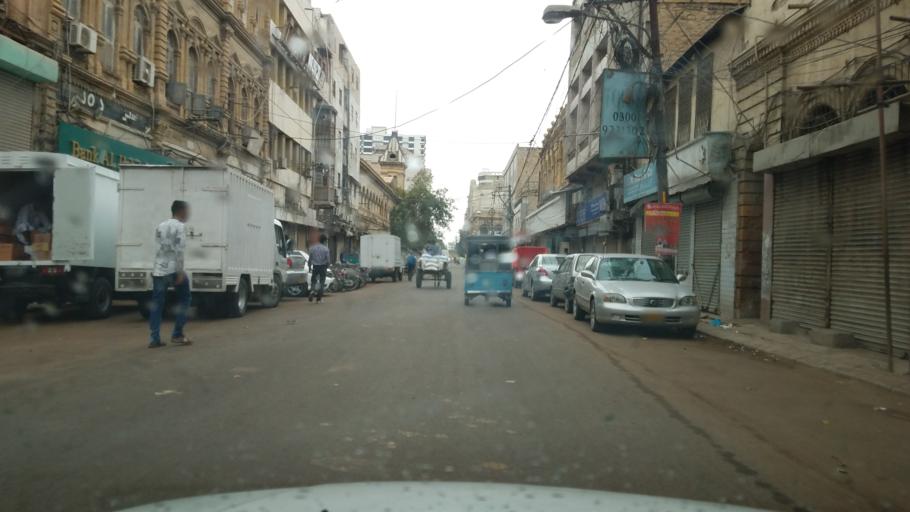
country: PK
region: Sindh
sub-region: Karachi District
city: Karachi
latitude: 24.8548
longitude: 67.0049
